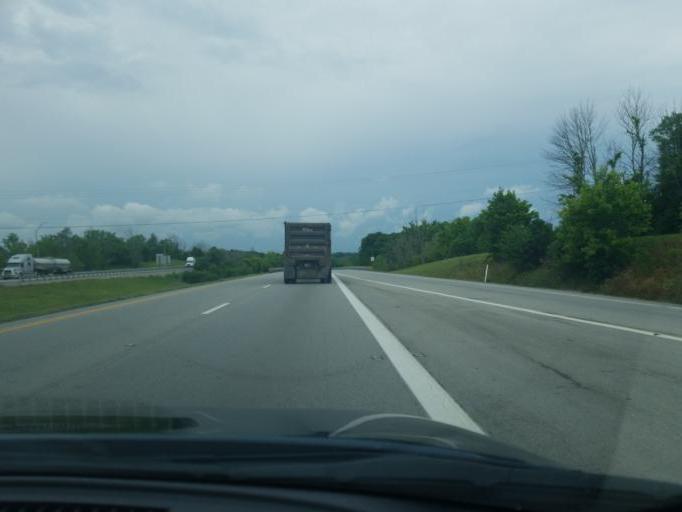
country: US
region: Kentucky
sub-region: Trimble County
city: Providence
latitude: 38.5189
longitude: -85.2357
